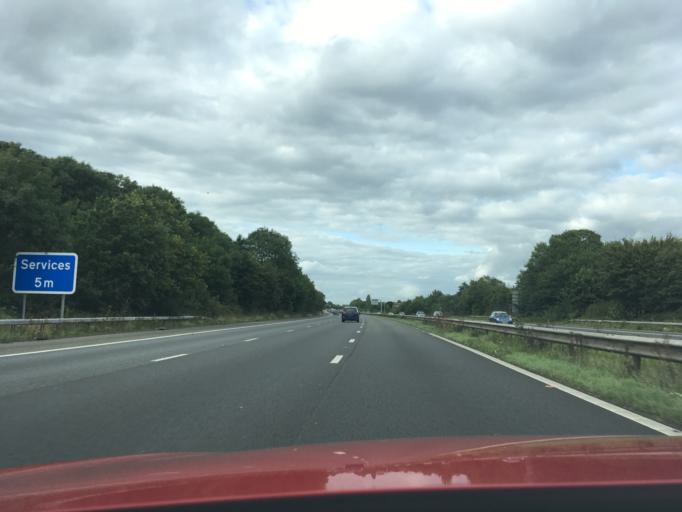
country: GB
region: England
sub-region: Gloucestershire
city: Stonehouse
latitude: 51.7688
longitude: -2.3132
